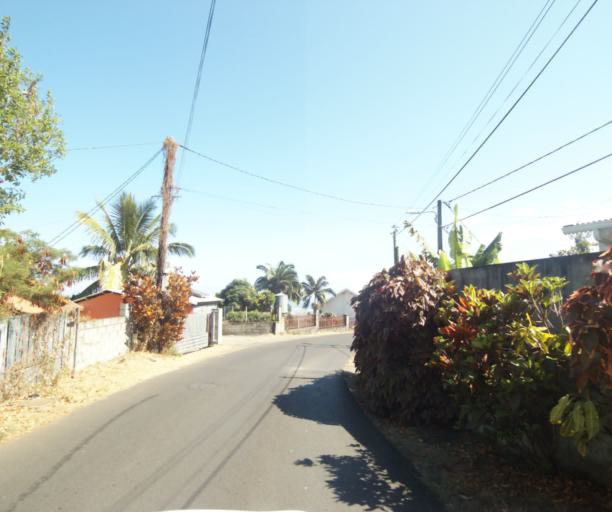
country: RE
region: Reunion
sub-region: Reunion
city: Saint-Paul
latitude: -20.9932
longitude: 55.3259
